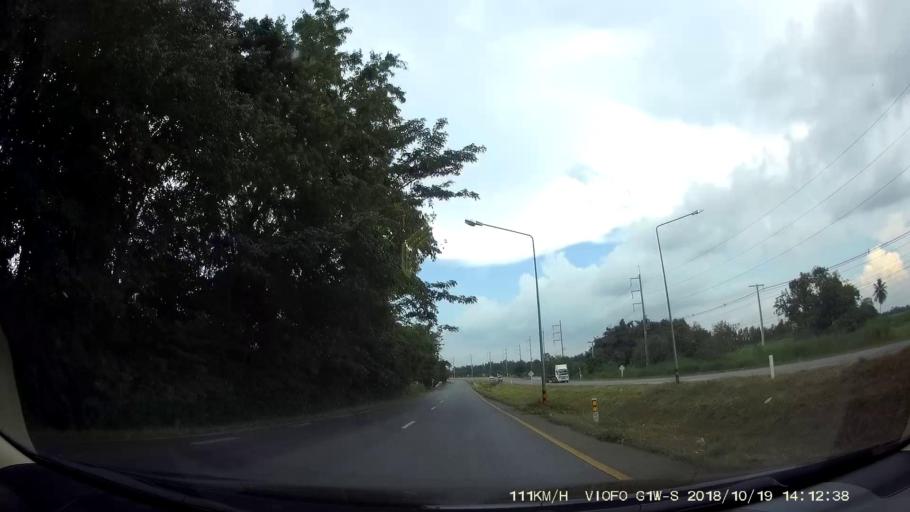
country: TH
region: Chaiyaphum
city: Khon Sawan
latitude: 15.9504
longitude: 102.1755
